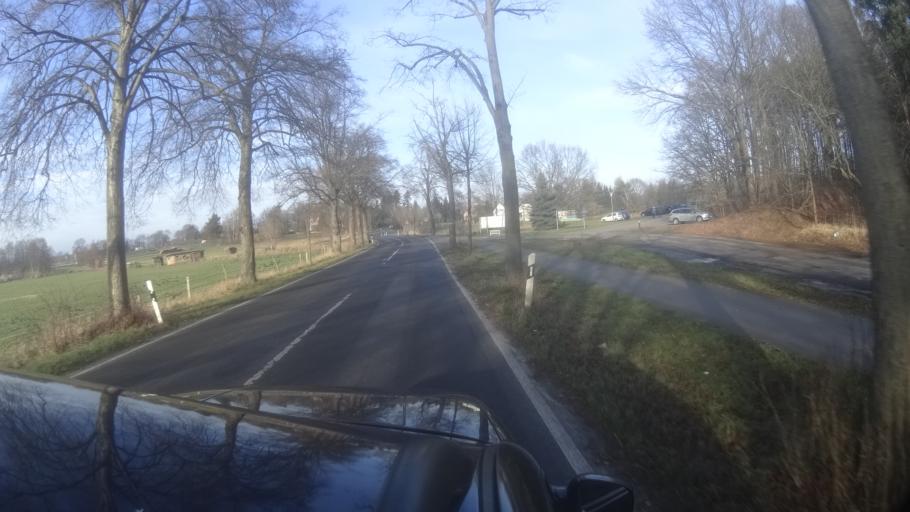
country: DE
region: Brandenburg
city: Kremmen
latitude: 52.8106
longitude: 13.0212
